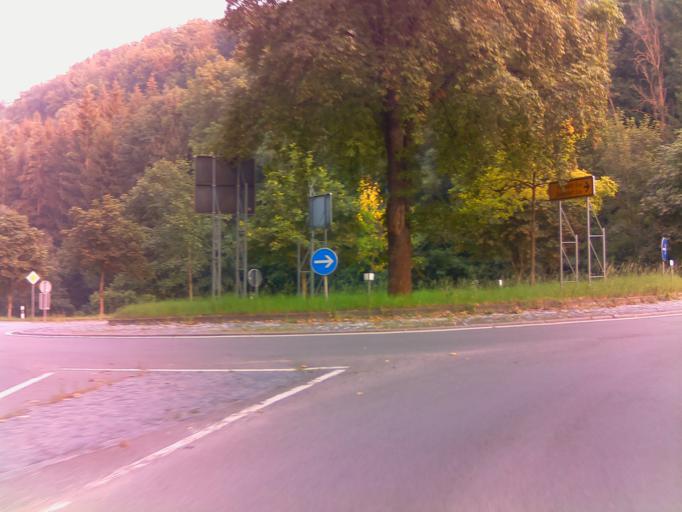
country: DE
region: Thuringia
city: Troistedt
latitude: 50.9170
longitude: 11.2554
